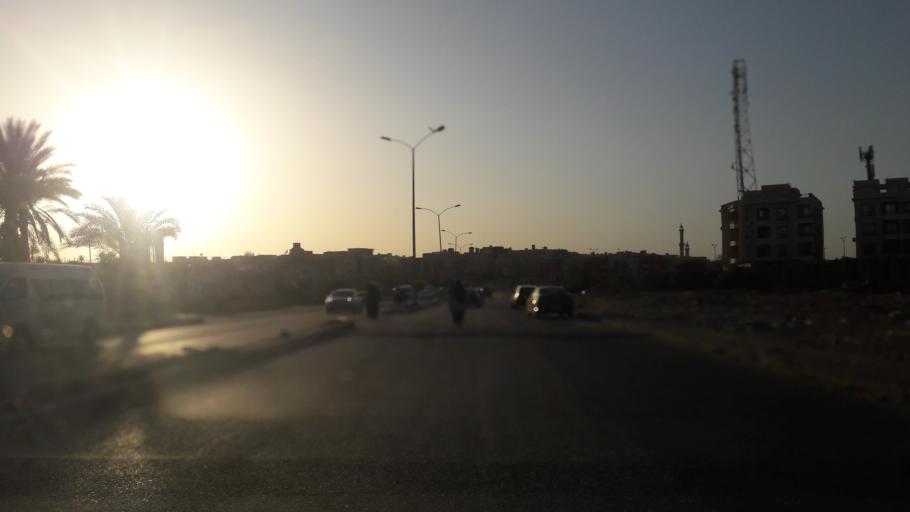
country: EG
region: Al Jizah
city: Madinat Sittah Uktubar
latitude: 29.9487
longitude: 30.9407
